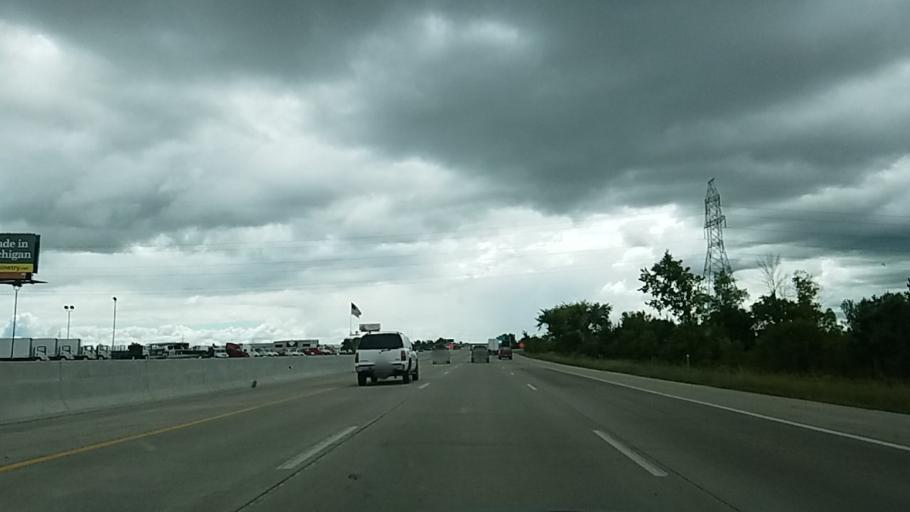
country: US
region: Michigan
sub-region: Saginaw County
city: Zilwaukee
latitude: 43.4572
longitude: -83.8910
